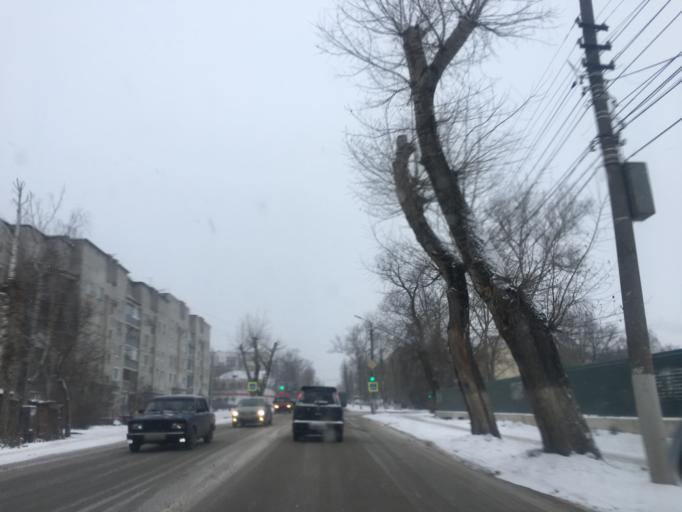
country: RU
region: Tula
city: Tula
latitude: 54.1951
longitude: 37.5653
